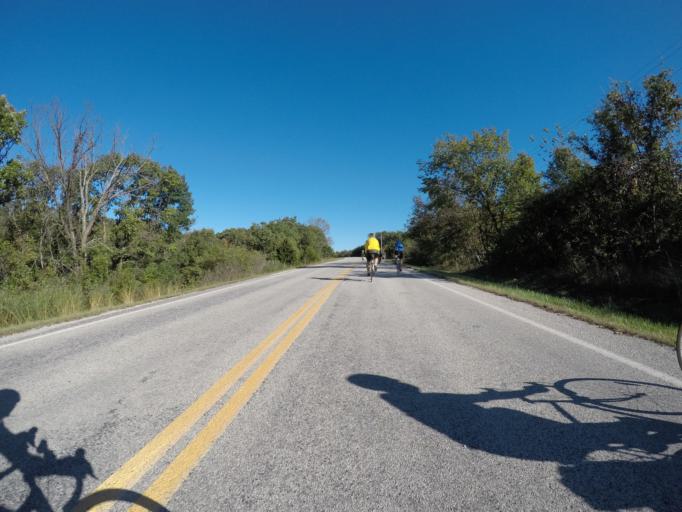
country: US
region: Kansas
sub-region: Johnson County
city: De Soto
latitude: 39.0034
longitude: -94.9733
